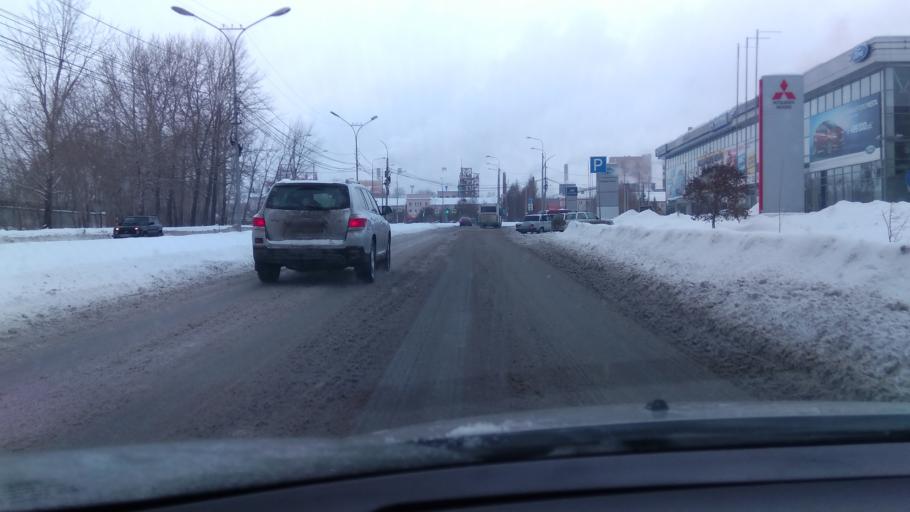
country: RU
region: Sverdlovsk
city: Nizhniy Tagil
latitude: 57.9073
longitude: 60.0092
